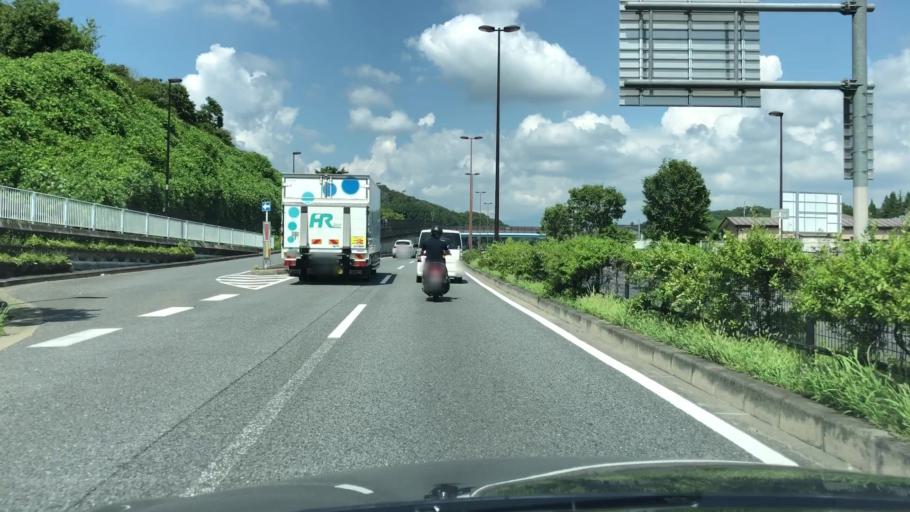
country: JP
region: Tokyo
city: Fussa
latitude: 35.7075
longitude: 139.2937
